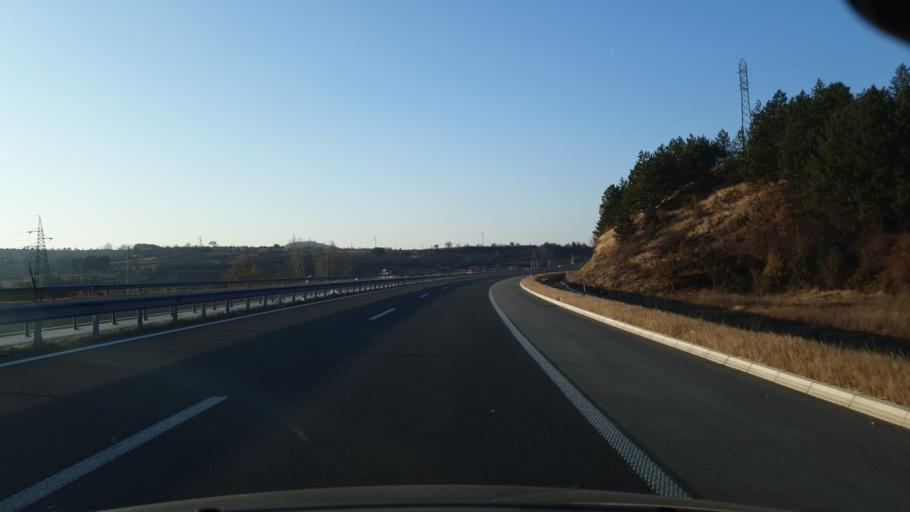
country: RS
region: Central Serbia
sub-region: Pirotski Okrug
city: Dimitrovgrad
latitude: 43.0240
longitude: 22.7273
